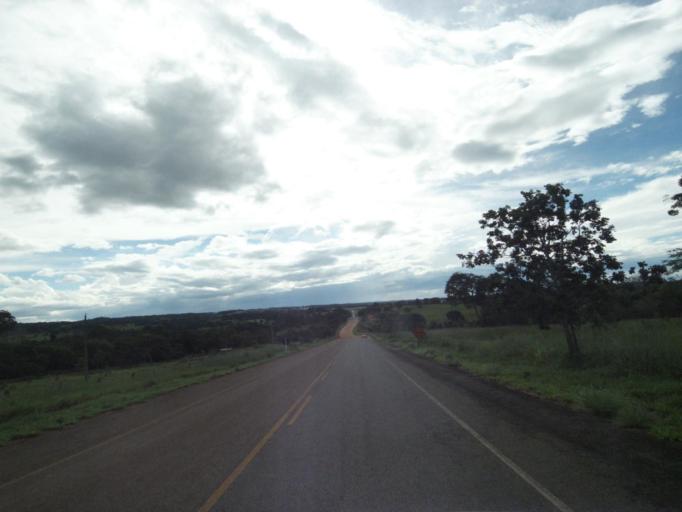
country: BR
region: Goias
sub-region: Jaragua
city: Jaragua
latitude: -15.8432
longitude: -49.3325
